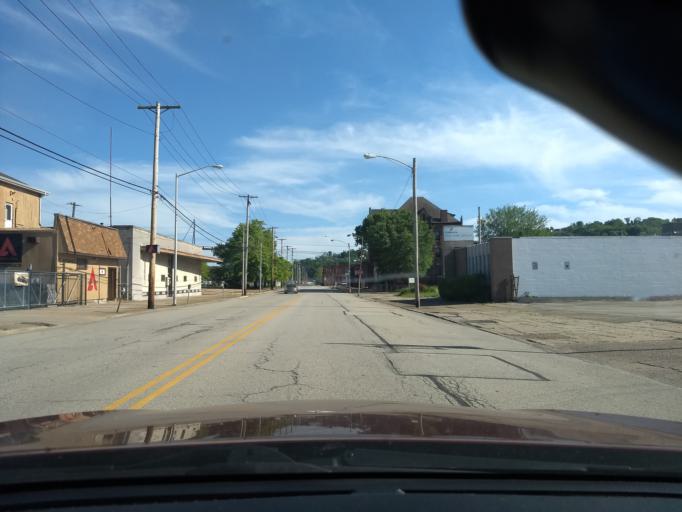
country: US
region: Pennsylvania
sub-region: Allegheny County
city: McKeesport
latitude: 40.3495
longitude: -79.8664
